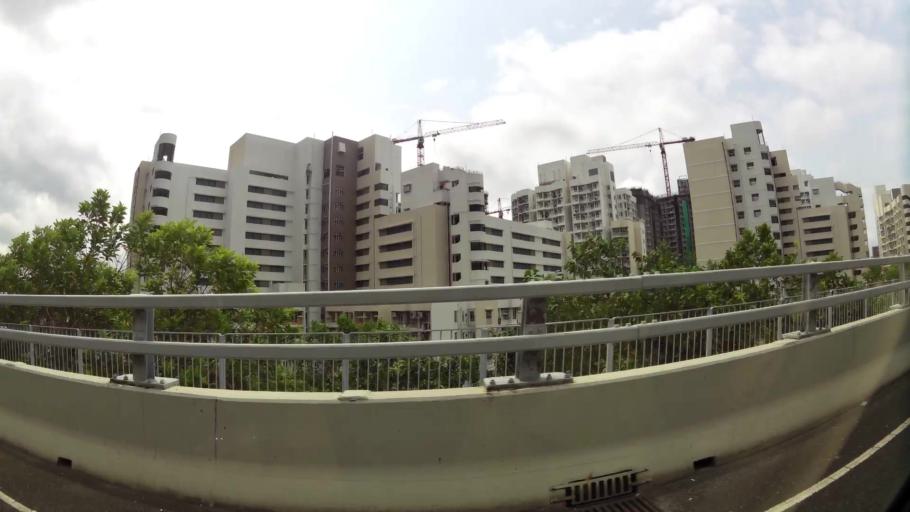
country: HK
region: Sham Shui Po
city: Sham Shui Po
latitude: 22.3426
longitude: 114.1572
